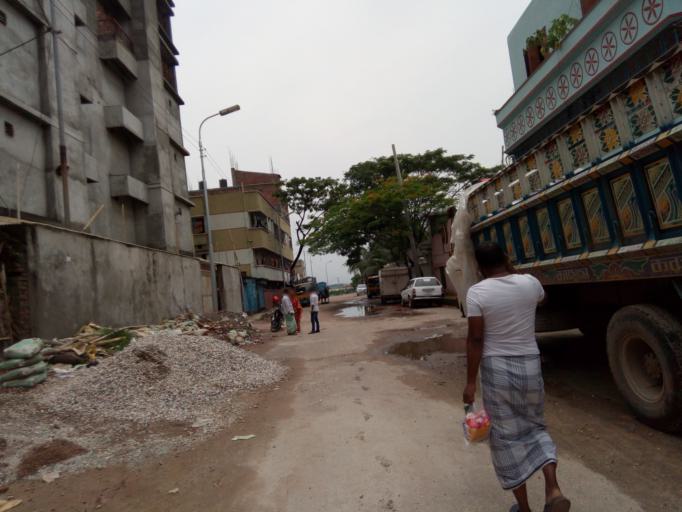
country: BD
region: Dhaka
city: Azimpur
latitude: 23.7629
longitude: 90.3403
